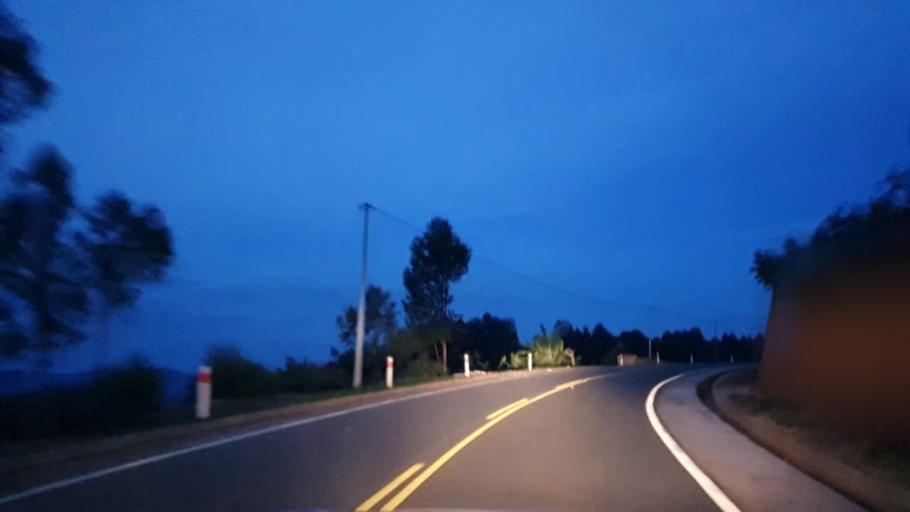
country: RW
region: Southern Province
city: Gikongoro
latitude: -2.4657
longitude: 29.5727
